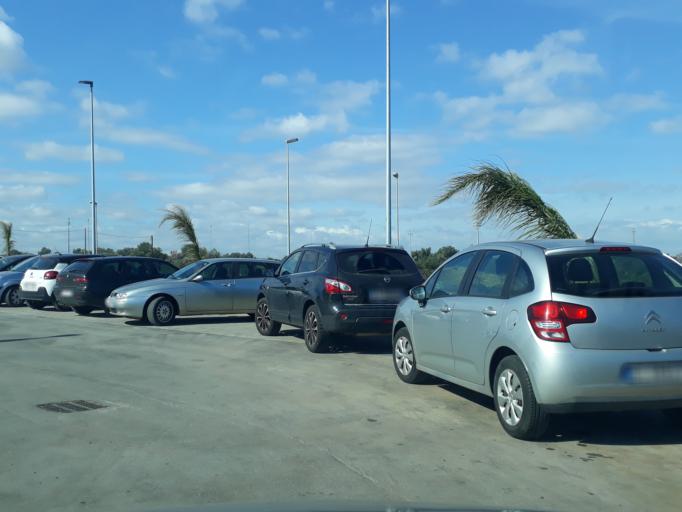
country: IT
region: Apulia
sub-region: Provincia di Bari
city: Monopoli
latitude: 40.9709
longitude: 17.2638
